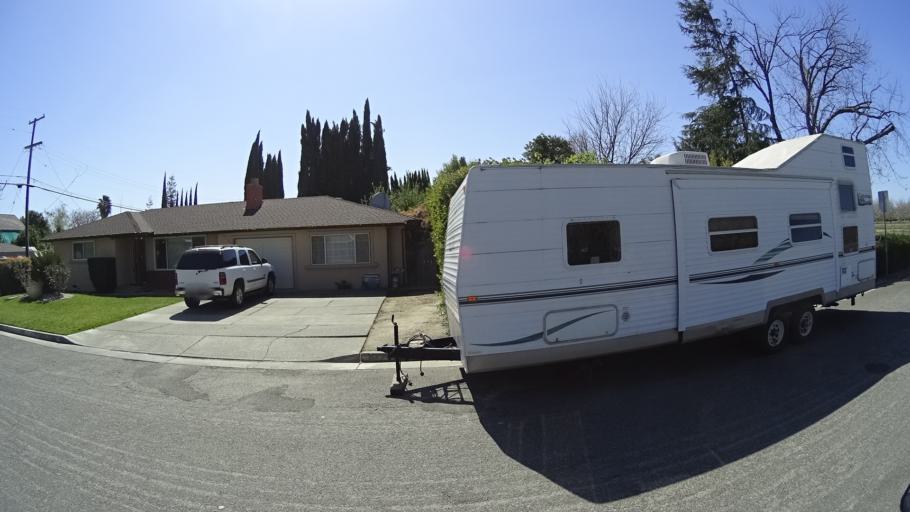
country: US
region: California
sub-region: Glenn County
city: Hamilton City
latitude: 39.7430
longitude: -122.0184
